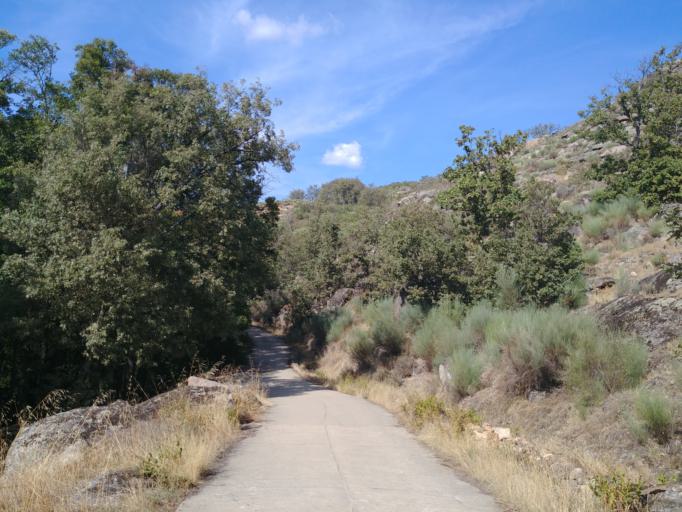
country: ES
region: Extremadura
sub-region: Provincia de Caceres
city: Garganta la Olla
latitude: 40.0979
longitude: -5.7695
